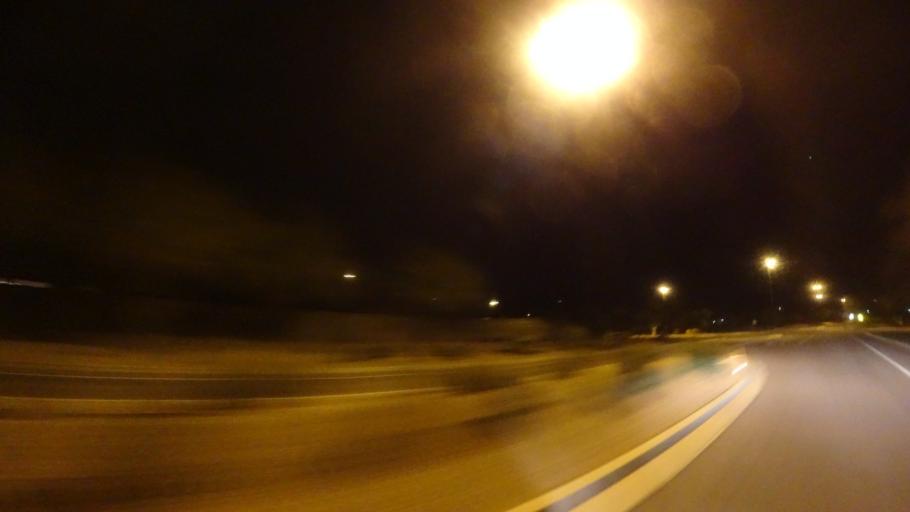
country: US
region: Arizona
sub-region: Maricopa County
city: Queen Creek
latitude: 33.2737
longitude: -111.7023
